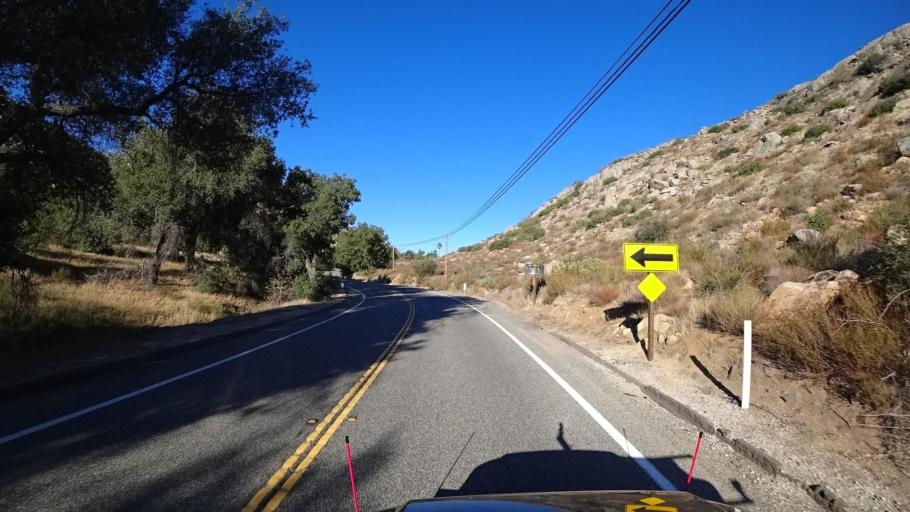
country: MX
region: Baja California
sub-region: Tecate
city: Hacienda Tecate
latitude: 32.5962
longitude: -116.5430
